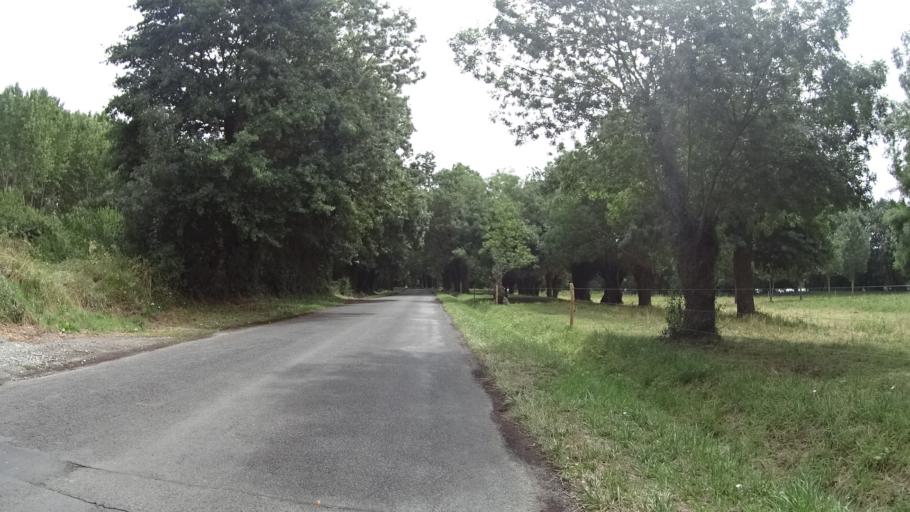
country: FR
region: Pays de la Loire
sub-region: Departement de Maine-et-Loire
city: Bouchemaine
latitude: 47.4176
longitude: -0.5914
